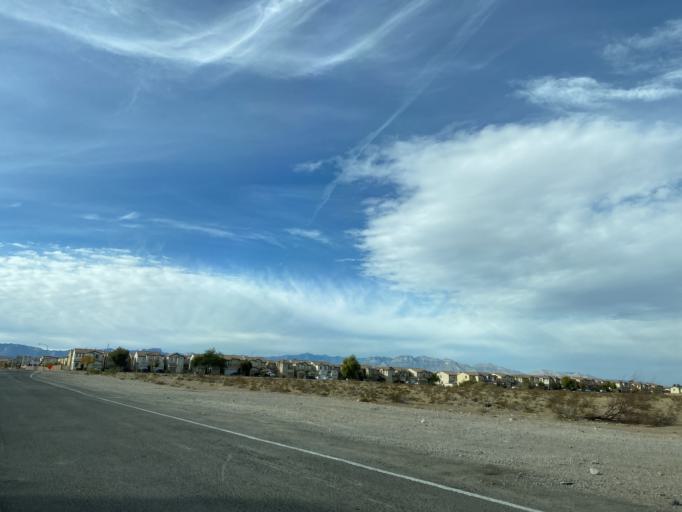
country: US
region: Nevada
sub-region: Clark County
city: Enterprise
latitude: 36.0424
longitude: -115.2190
